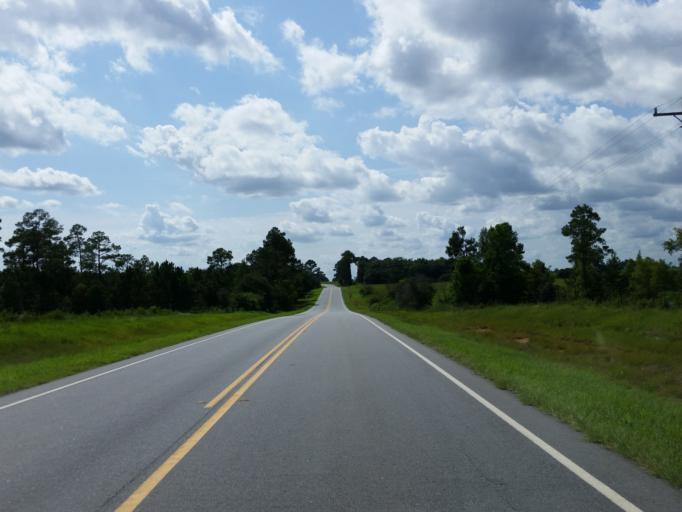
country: US
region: Georgia
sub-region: Turner County
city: Ashburn
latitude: 31.6554
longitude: -83.5562
